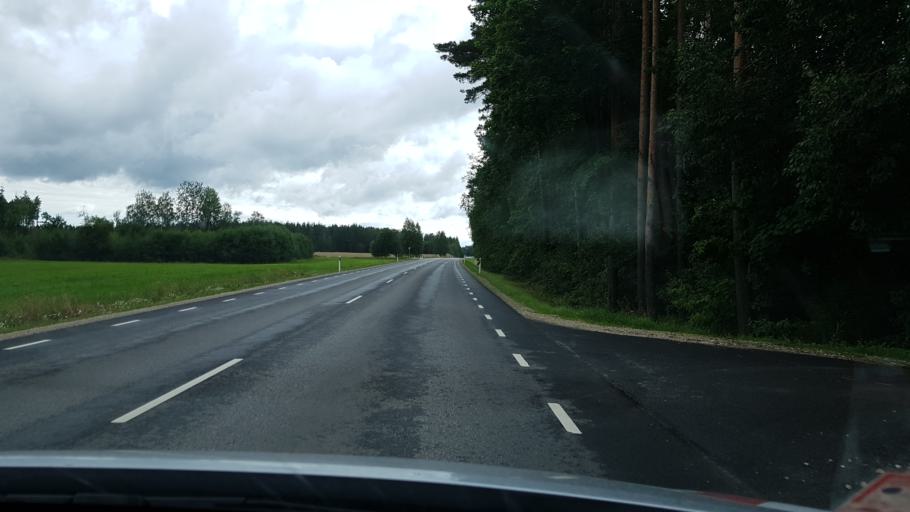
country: EE
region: Polvamaa
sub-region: Polva linn
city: Polva
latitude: 58.0422
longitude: 27.0931
